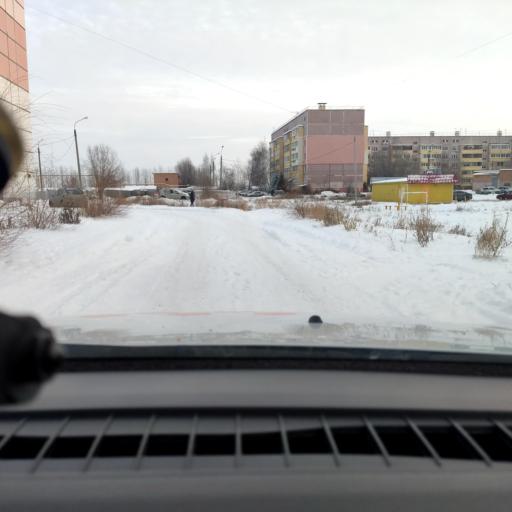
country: RU
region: Samara
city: Samara
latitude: 53.1100
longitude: 50.0836
